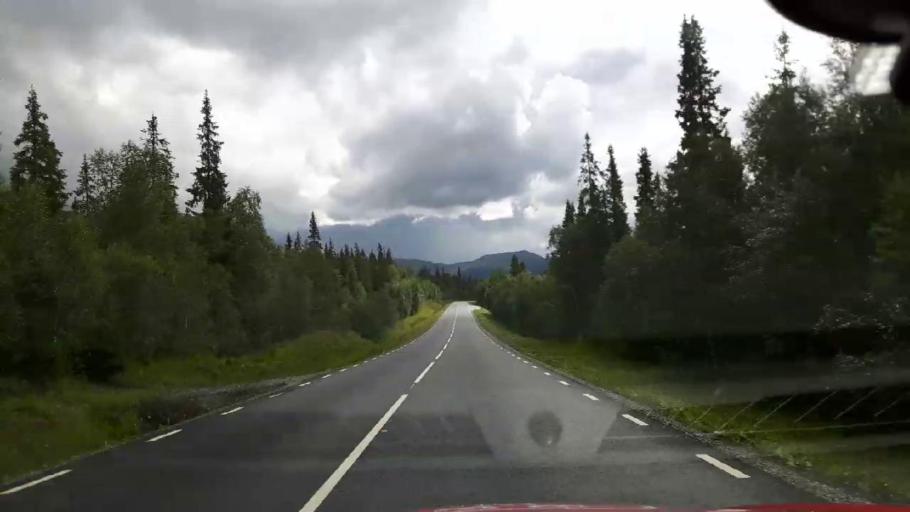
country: NO
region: Nord-Trondelag
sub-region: Royrvik
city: Royrvik
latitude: 64.8813
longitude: 14.2095
